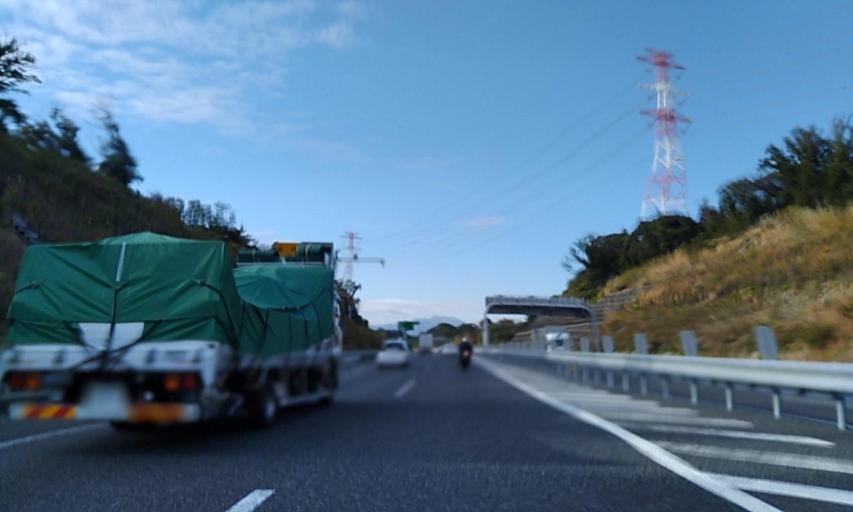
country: JP
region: Mie
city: Yokkaichi
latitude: 35.0443
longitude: 136.6186
